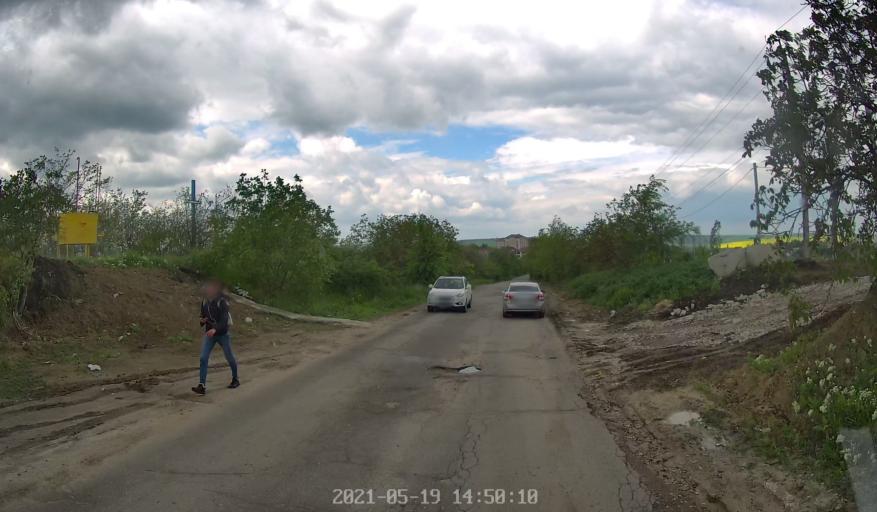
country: MD
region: Chisinau
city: Stauceni
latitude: 47.0544
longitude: 28.9471
